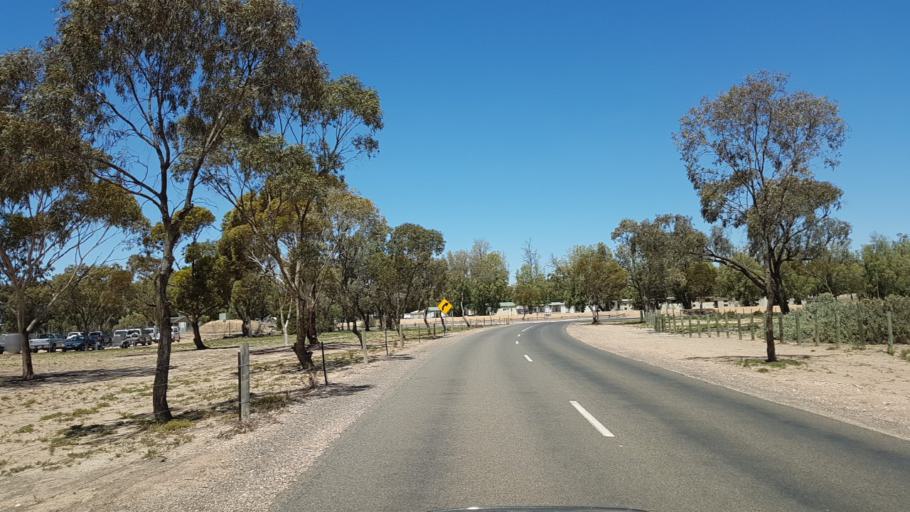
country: AU
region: South Australia
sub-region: Loxton Waikerie
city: Waikerie
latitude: -34.1726
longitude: 139.9807
